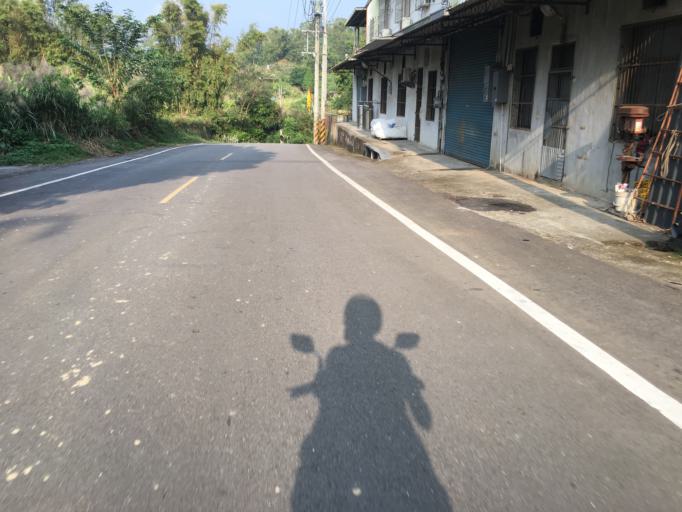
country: TW
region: Taiwan
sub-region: Hsinchu
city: Hsinchu
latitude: 24.7052
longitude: 121.0544
